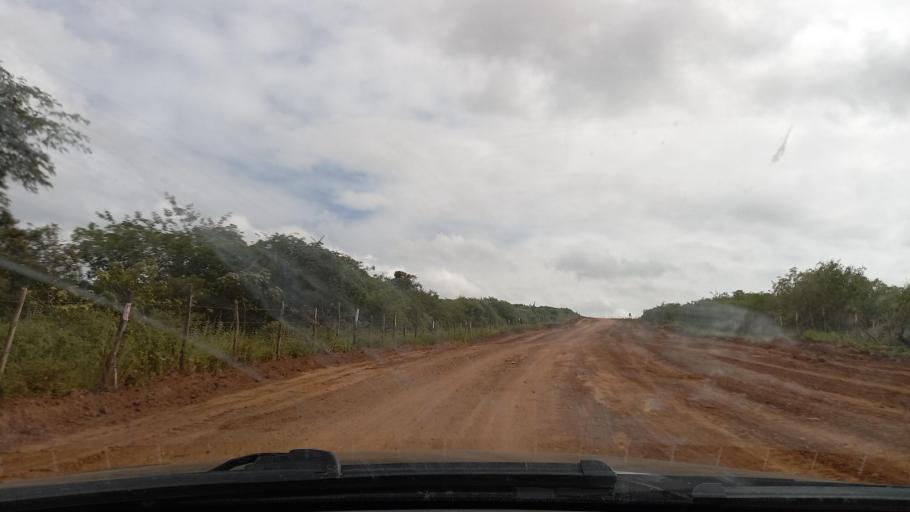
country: BR
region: Sergipe
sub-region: Caninde De Sao Francisco
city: Caninde de Sao Francisco
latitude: -9.6185
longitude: -37.7600
